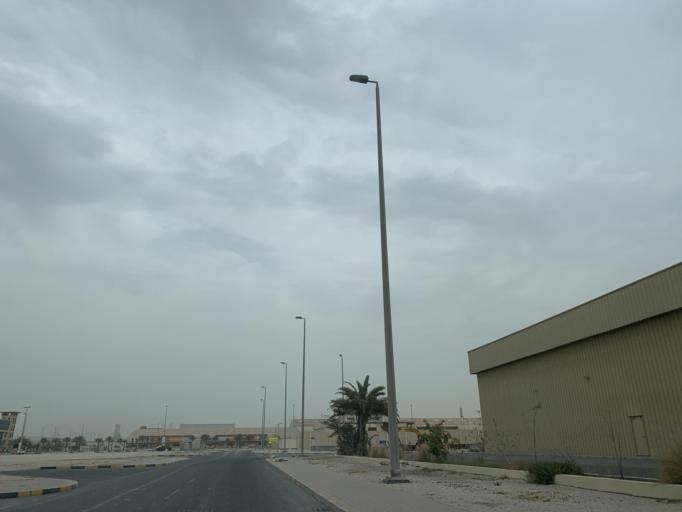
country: BH
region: Muharraq
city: Al Hadd
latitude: 26.2229
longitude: 50.6729
